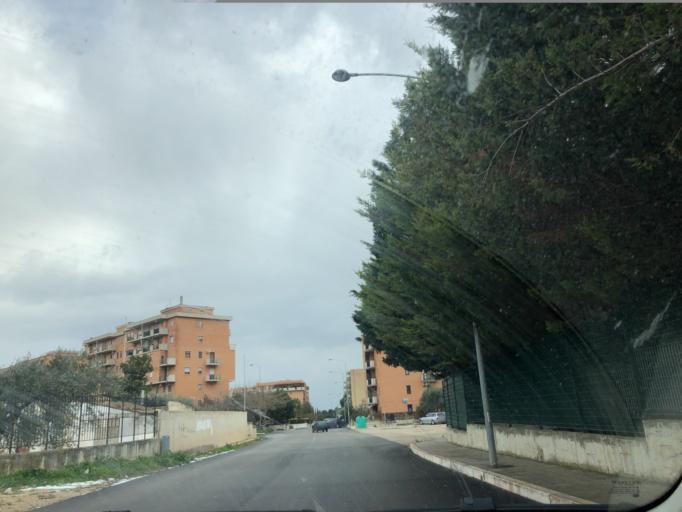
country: IT
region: Apulia
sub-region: Provincia di Foggia
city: Lucera
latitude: 41.5003
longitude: 15.3512
